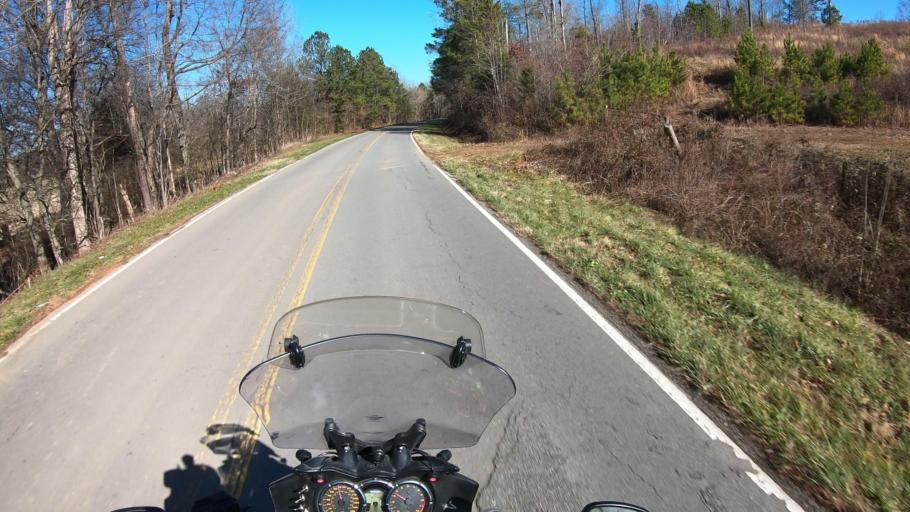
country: US
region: Georgia
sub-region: Bartow County
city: Rydal
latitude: 34.3369
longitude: -84.7536
